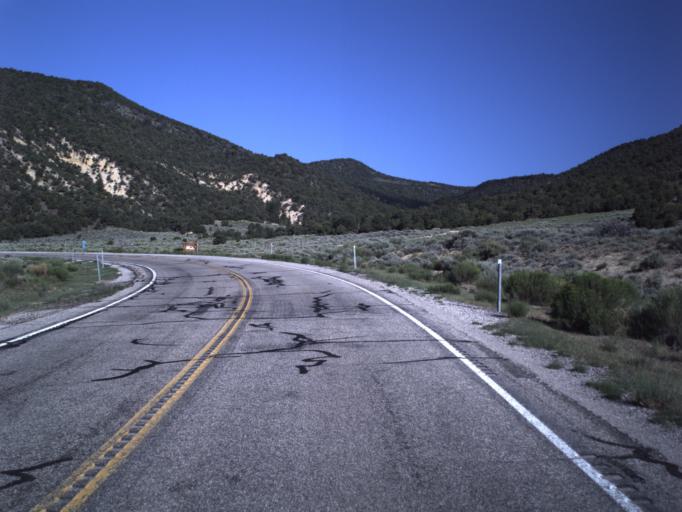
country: US
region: Utah
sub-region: Wayne County
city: Loa
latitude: 38.6721
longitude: -111.4163
